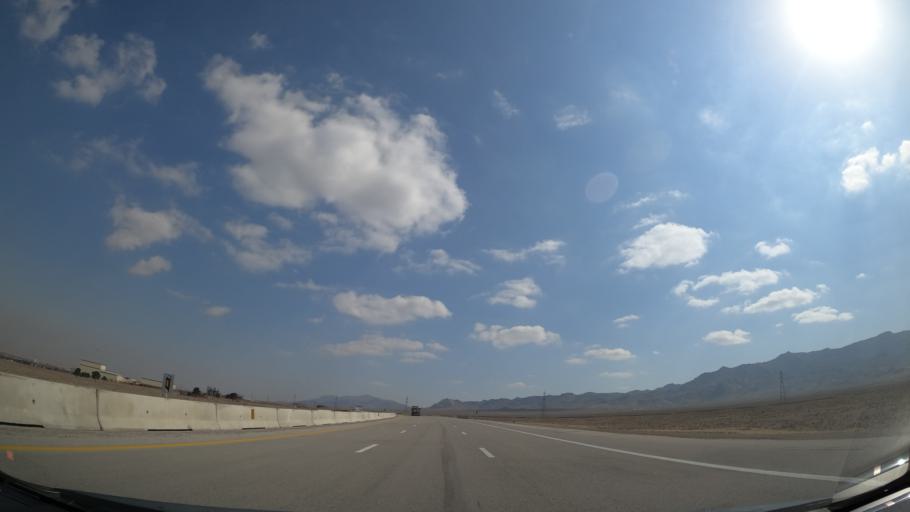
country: IR
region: Alborz
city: Eshtehard
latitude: 35.7186
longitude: 50.5729
